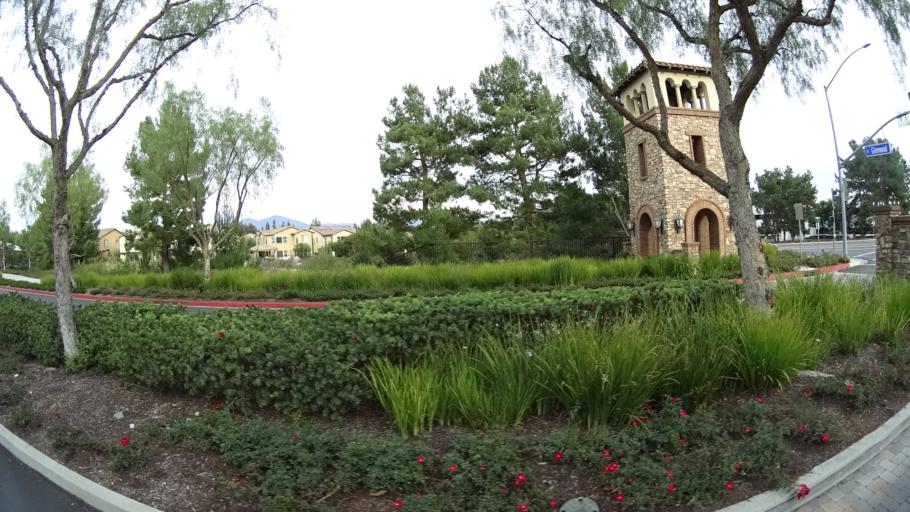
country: US
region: California
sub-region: Orange County
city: Laguna Woods
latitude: 33.5953
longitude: -117.7255
